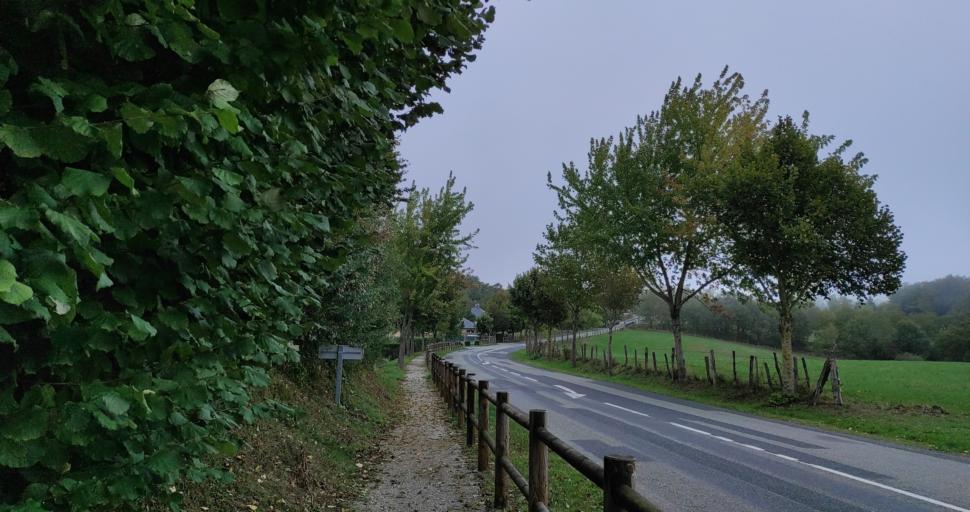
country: FR
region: Midi-Pyrenees
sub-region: Departement de l'Aveyron
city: Baraqueville
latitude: 44.2701
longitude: 2.4349
